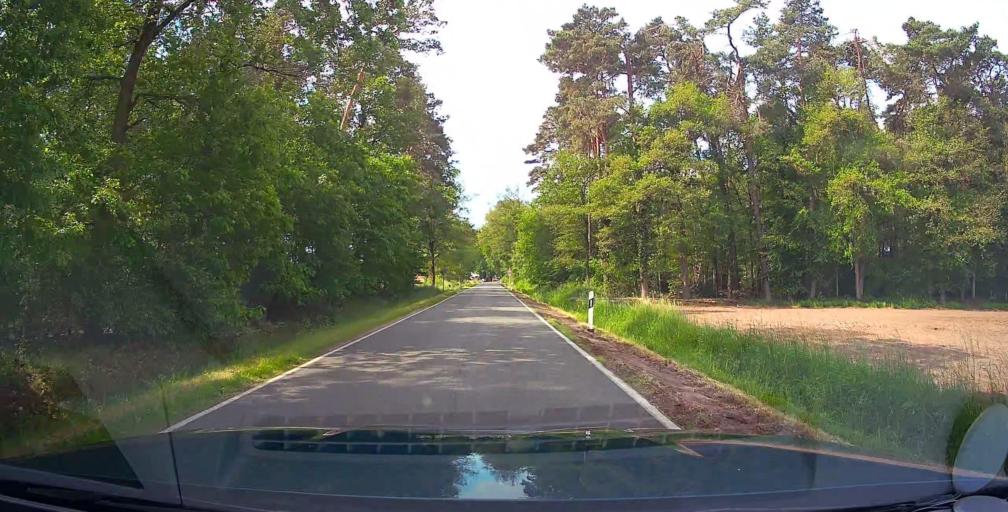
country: DE
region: North Rhine-Westphalia
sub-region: Regierungsbezirk Munster
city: Ladbergen
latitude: 52.1414
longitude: 7.7996
